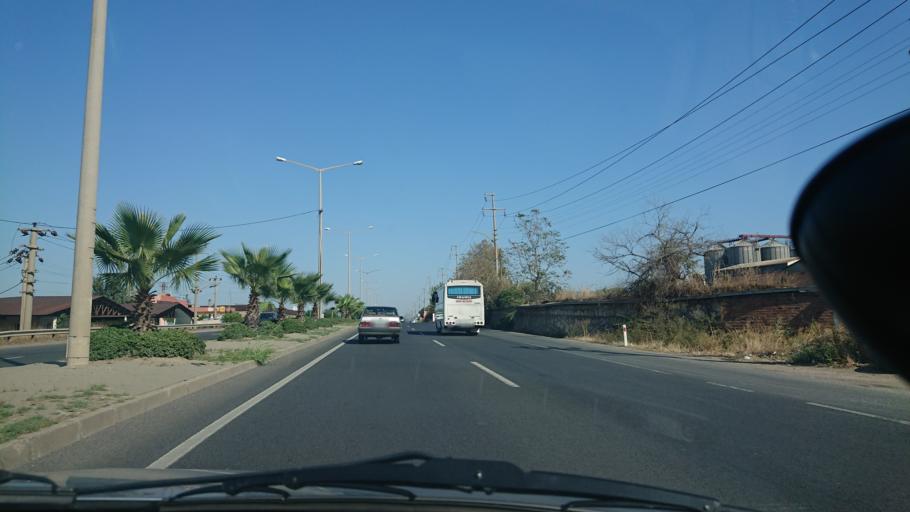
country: TR
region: Manisa
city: Turgutlu
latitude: 38.4957
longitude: 27.7431
